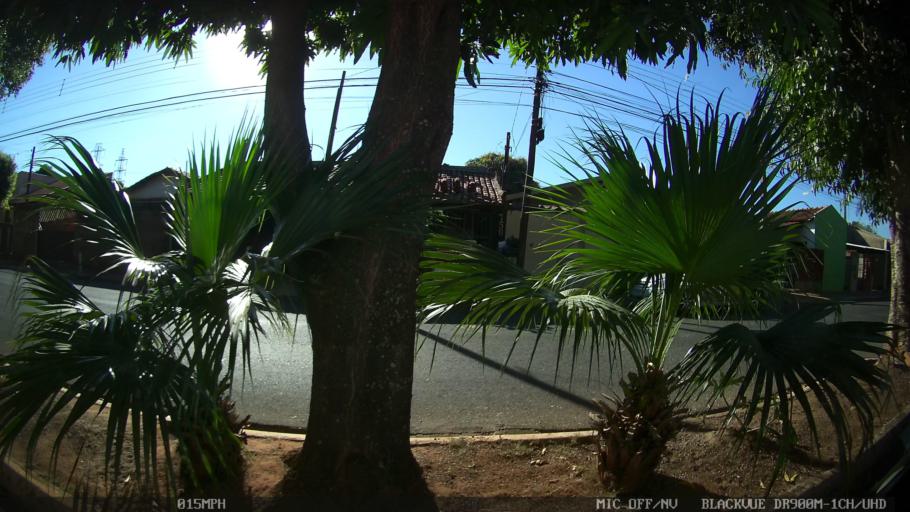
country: BR
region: Sao Paulo
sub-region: Olimpia
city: Olimpia
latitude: -20.7254
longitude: -48.8960
